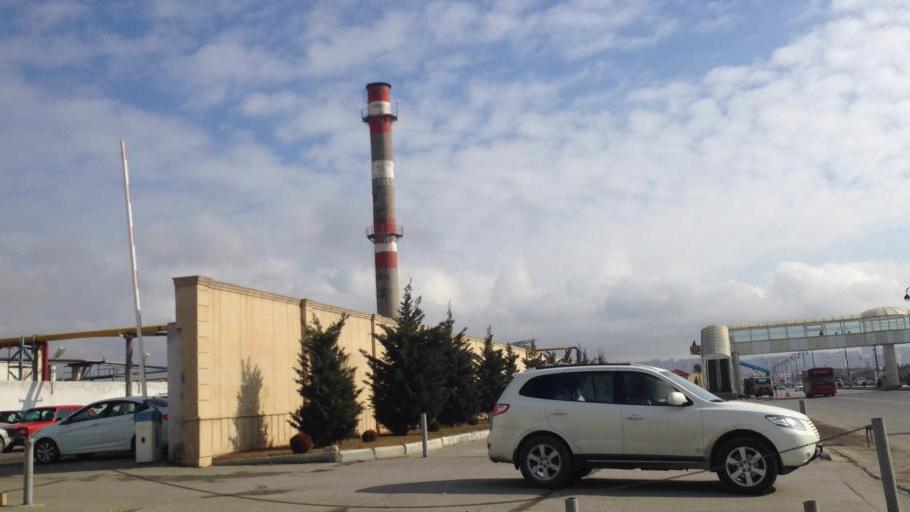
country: AZ
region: Baki
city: Baku
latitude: 40.3777
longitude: 49.9063
